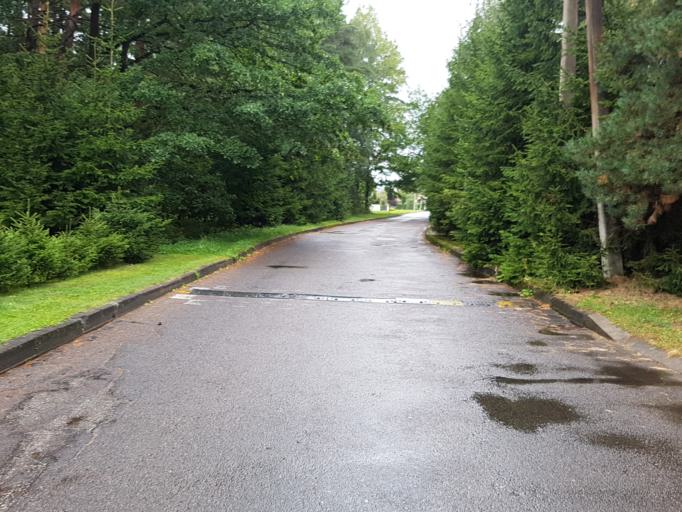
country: LT
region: Vilnius County
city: Lazdynai
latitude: 54.6611
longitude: 25.1852
